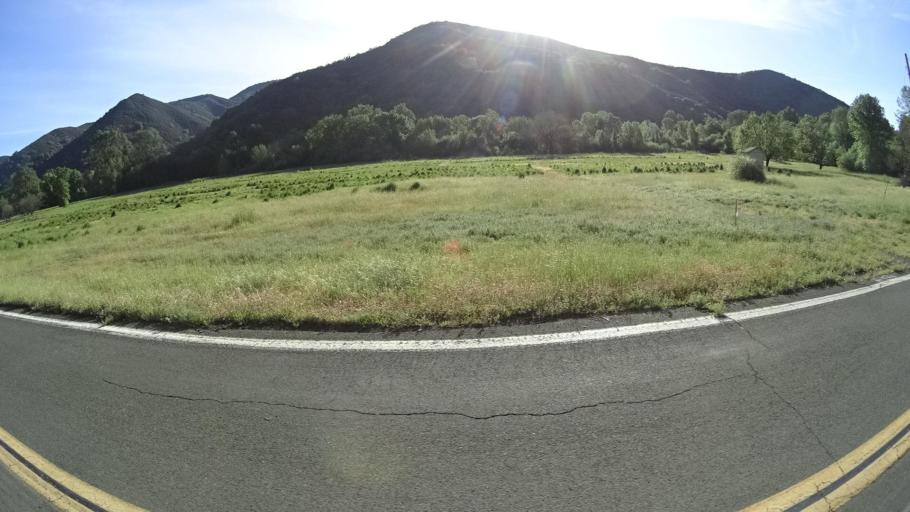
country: US
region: California
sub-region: Lake County
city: Upper Lake
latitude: 39.1315
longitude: -122.9978
